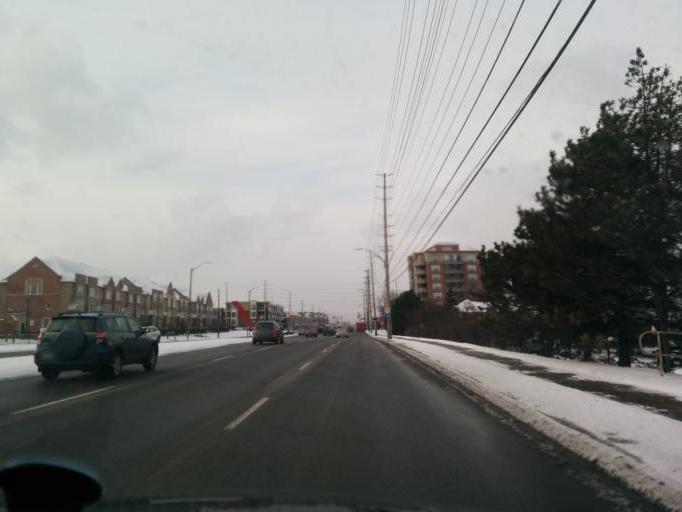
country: CA
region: Ontario
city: Mississauga
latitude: 43.5477
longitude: -79.7153
